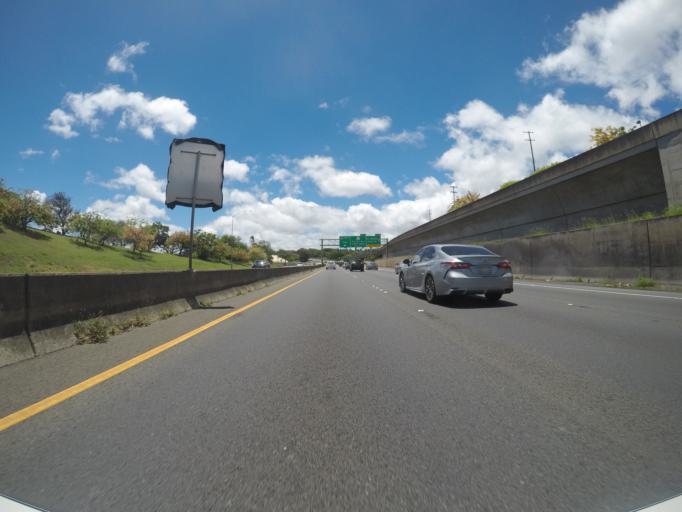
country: US
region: Hawaii
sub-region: Honolulu County
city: Honolulu
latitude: 21.3391
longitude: -157.8847
